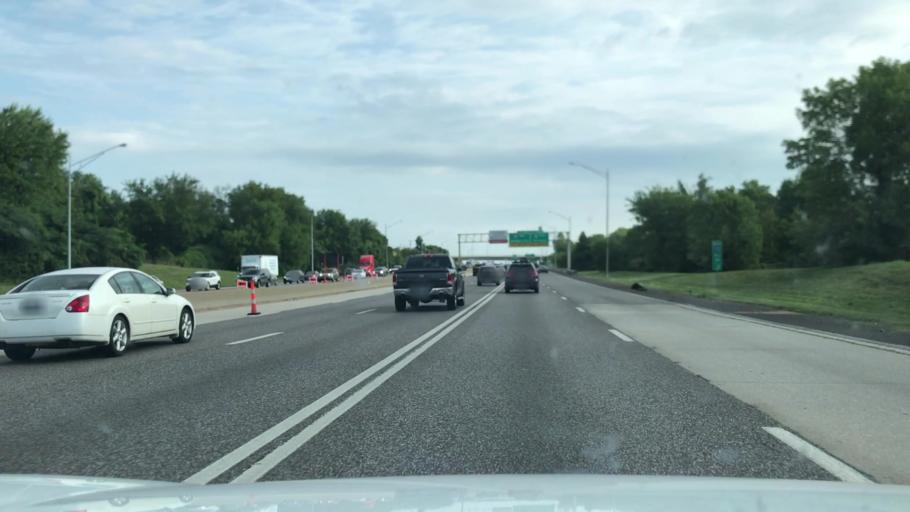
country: US
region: Missouri
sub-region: Saint Louis County
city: Maryland Heights
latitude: 38.7352
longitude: -90.4425
